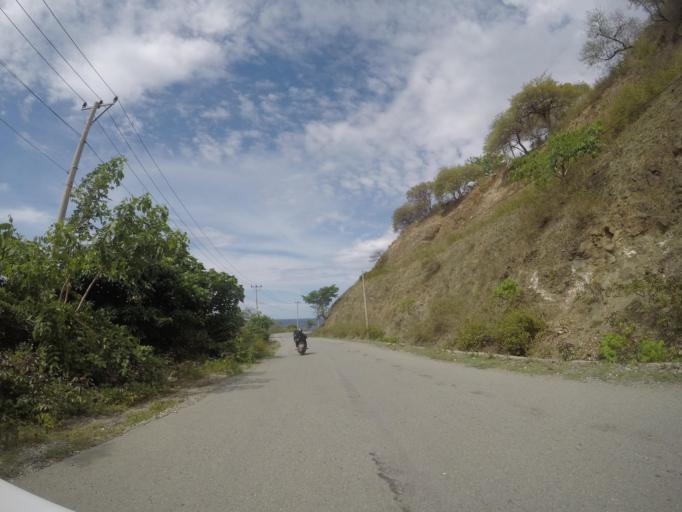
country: TL
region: Liquica
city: Maubara
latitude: -8.6276
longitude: 125.1588
